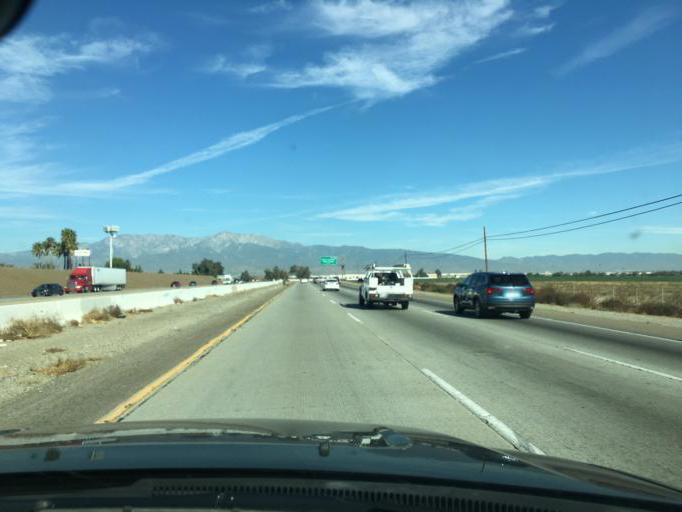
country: US
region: California
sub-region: Riverside County
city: Mira Loma
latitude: 33.9823
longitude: -117.5488
